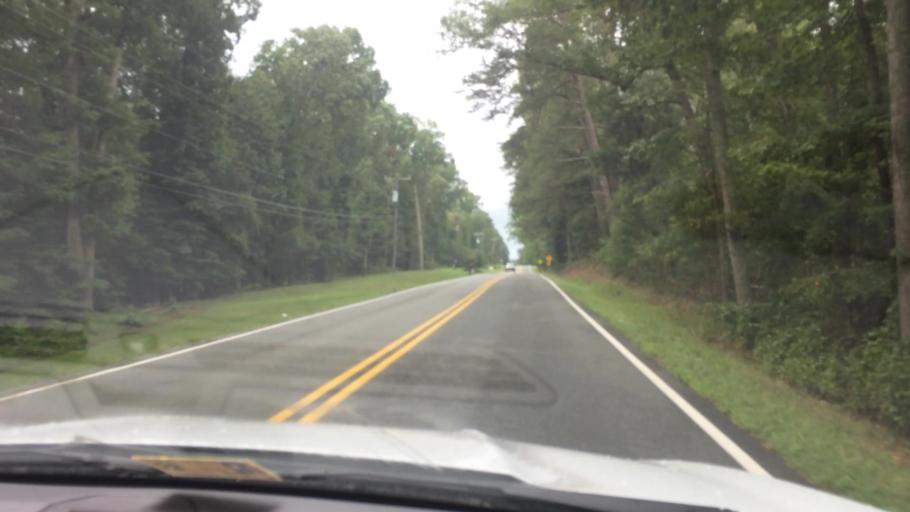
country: US
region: Virginia
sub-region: New Kent County
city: New Kent
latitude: 37.4727
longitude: -77.0325
